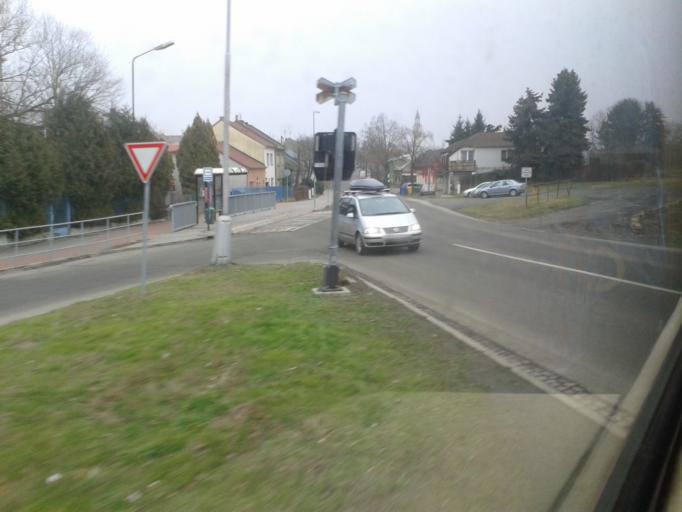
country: CZ
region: Olomoucky
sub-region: Okres Olomouc
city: Olomouc
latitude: 49.6090
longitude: 17.2280
